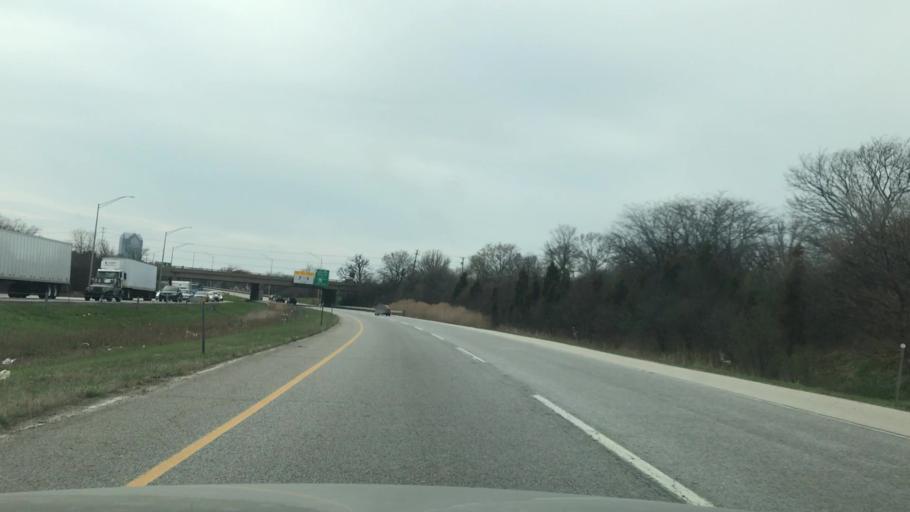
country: US
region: Illinois
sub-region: DuPage County
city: Oak Brook
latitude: 41.8530
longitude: -87.9283
